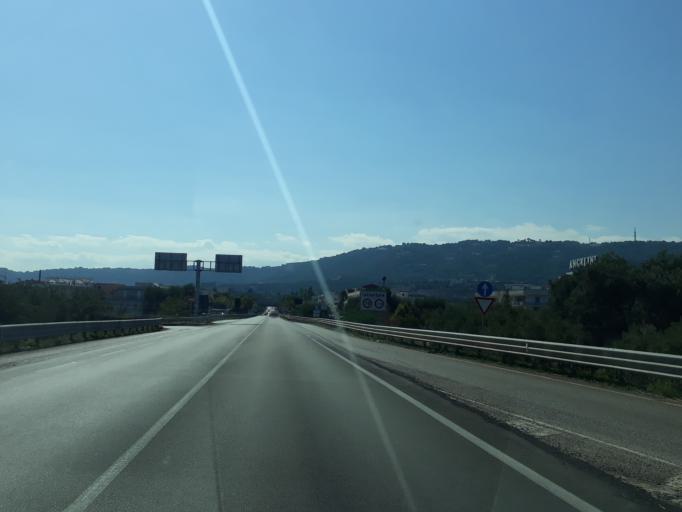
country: IT
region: Apulia
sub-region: Provincia di Brindisi
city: Fasano
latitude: 40.8464
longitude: 17.3553
